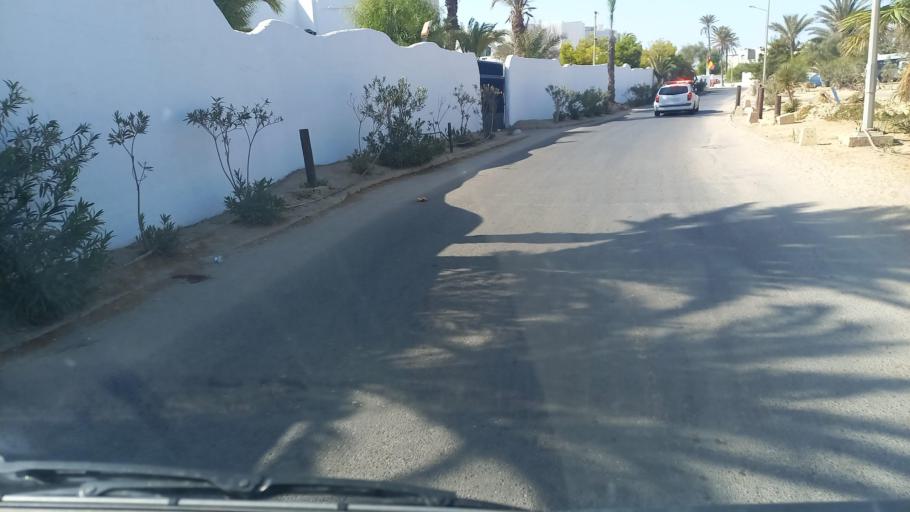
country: TN
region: Madanin
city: Midoun
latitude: 33.8506
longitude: 10.9889
